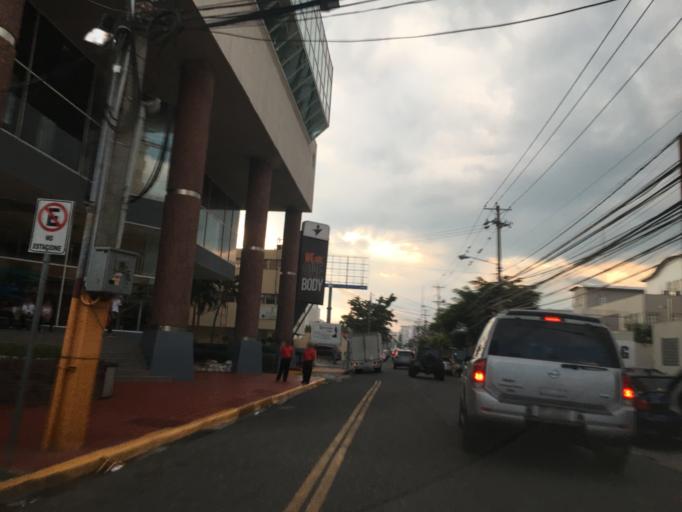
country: DO
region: Nacional
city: La Julia
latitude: 18.4764
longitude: -69.9286
